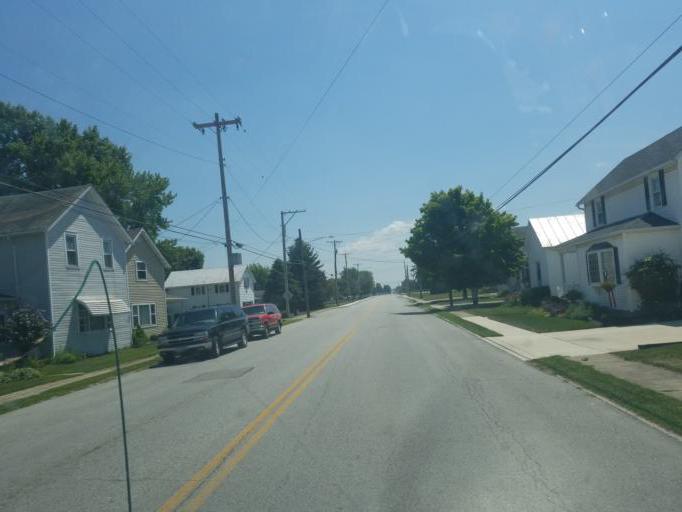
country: US
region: Ohio
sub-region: Shelby County
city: Botkins
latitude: 40.4666
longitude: -84.1820
